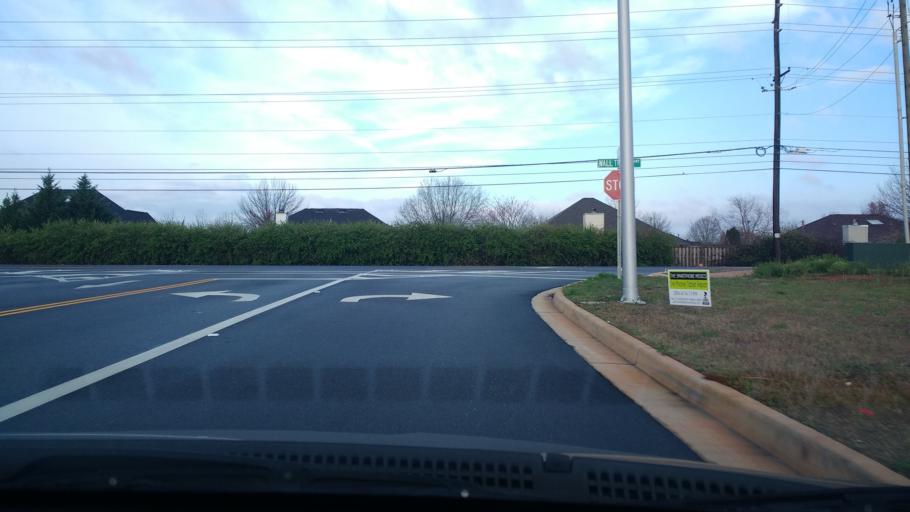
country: US
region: Alabama
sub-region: Madison County
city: Madison
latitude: 34.7089
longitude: -86.7505
